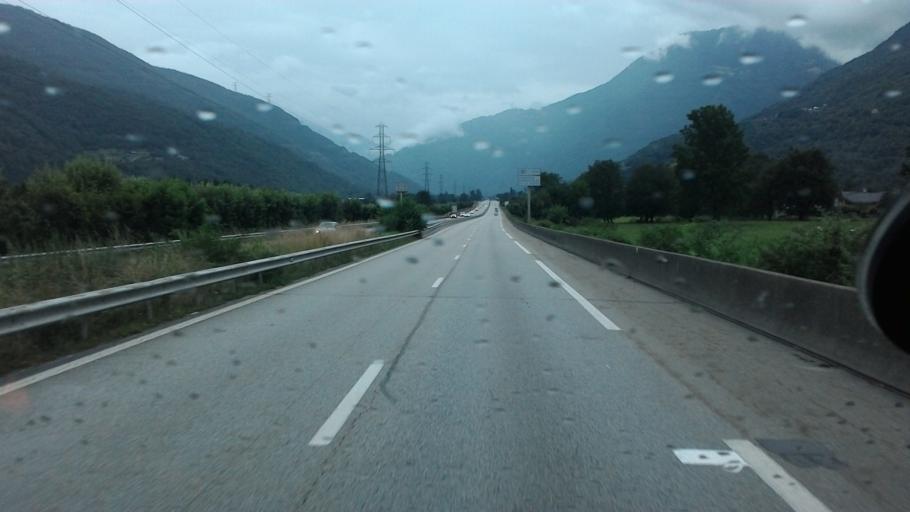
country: FR
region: Rhone-Alpes
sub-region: Departement de la Savoie
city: La Bathie
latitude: 45.6187
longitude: 6.4484
